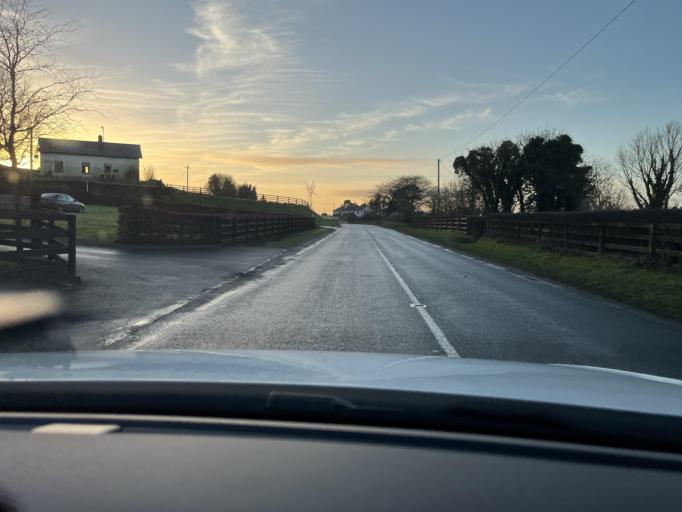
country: IE
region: Ulster
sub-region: An Cabhan
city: Ballyconnell
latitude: 54.0812
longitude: -7.6665
